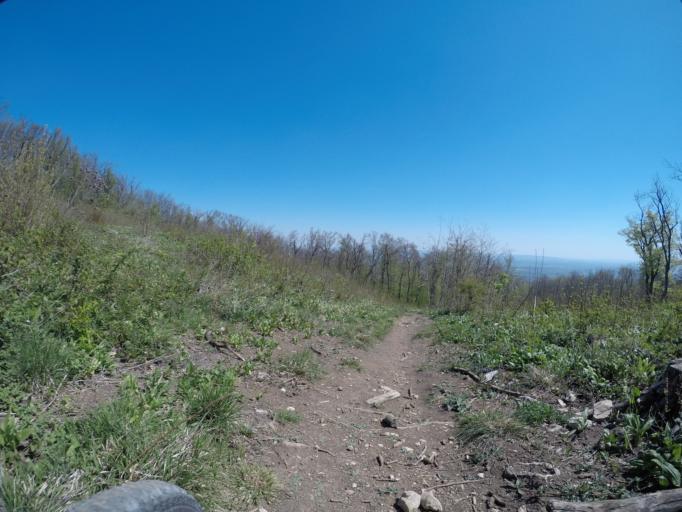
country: AT
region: Lower Austria
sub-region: Politischer Bezirk Modling
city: Gumpoldskirchen
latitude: 48.0515
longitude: 16.2519
